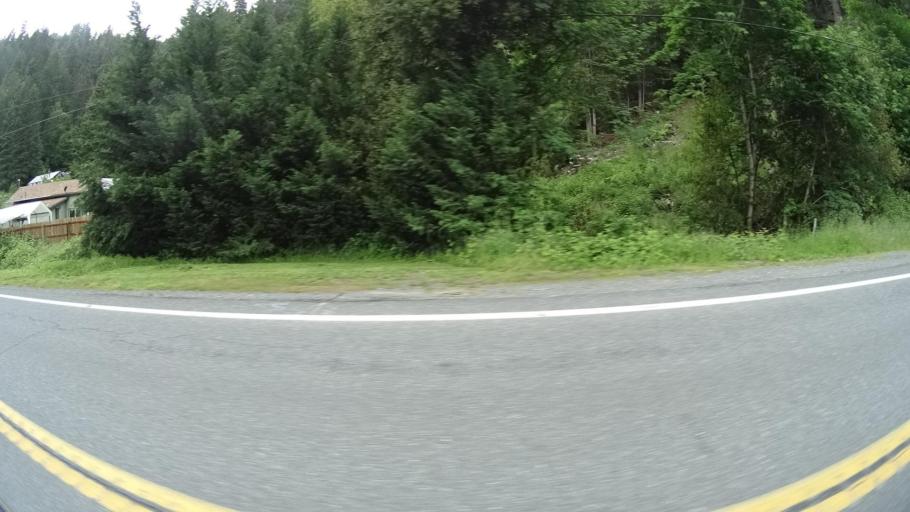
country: US
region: California
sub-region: Humboldt County
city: Willow Creek
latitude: 40.9782
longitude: -123.6417
